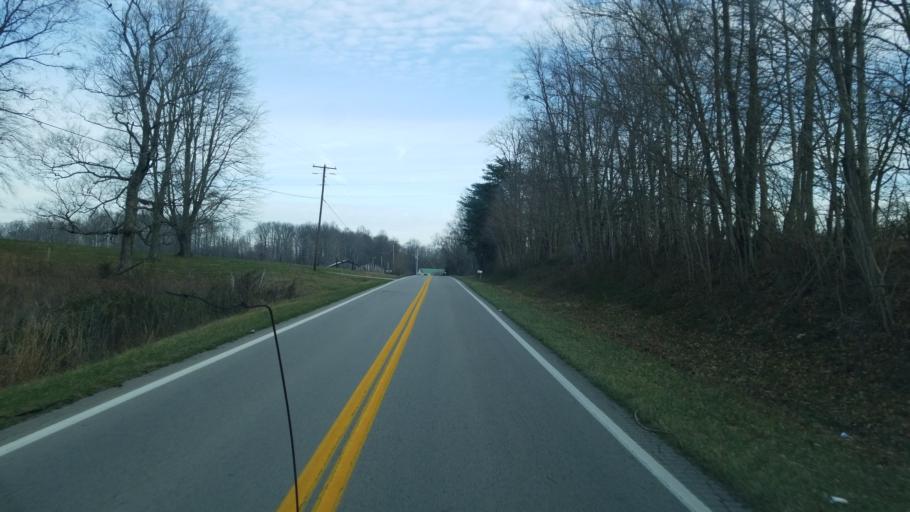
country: US
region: Kentucky
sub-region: Clinton County
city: Albany
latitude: 36.8068
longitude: -85.1805
